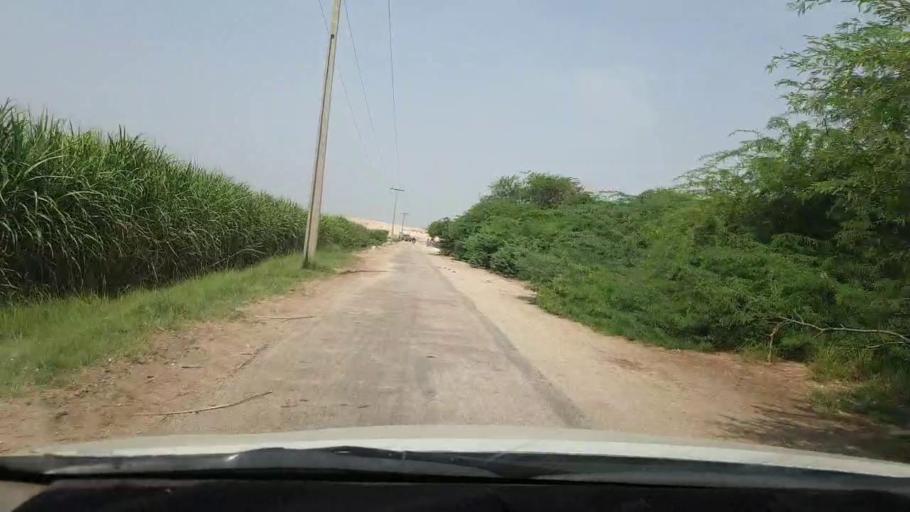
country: PK
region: Sindh
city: Rohri
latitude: 27.5957
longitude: 68.9805
